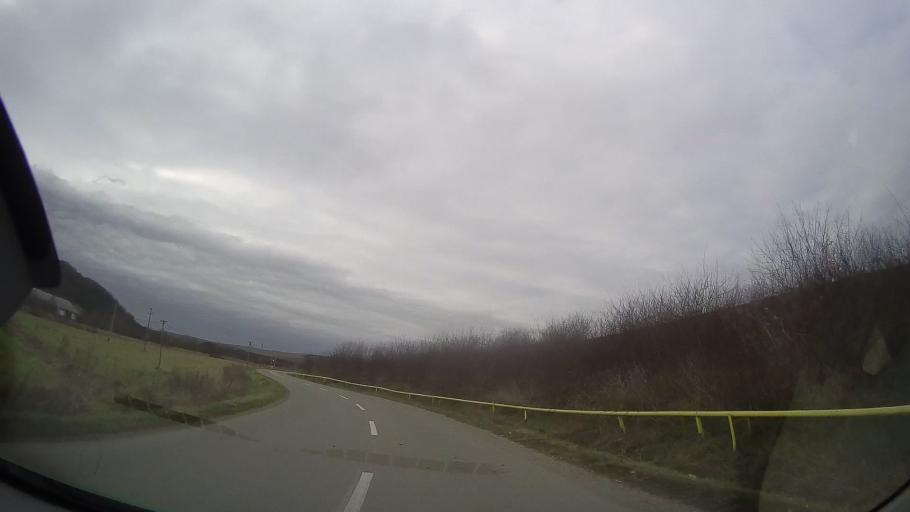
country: RO
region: Bistrita-Nasaud
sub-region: Comuna Milas
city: Milas
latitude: 46.8134
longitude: 24.4383
